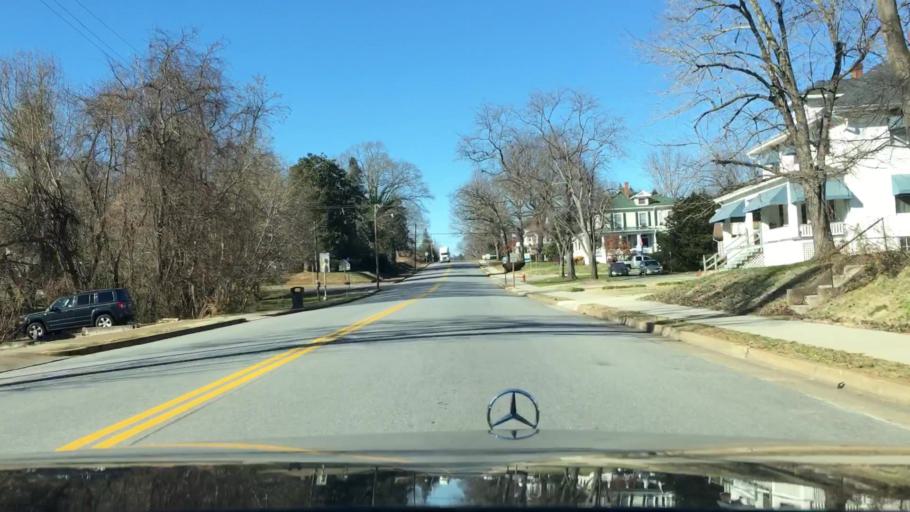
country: US
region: Virginia
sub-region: Campbell County
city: Altavista
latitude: 37.1115
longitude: -79.2957
